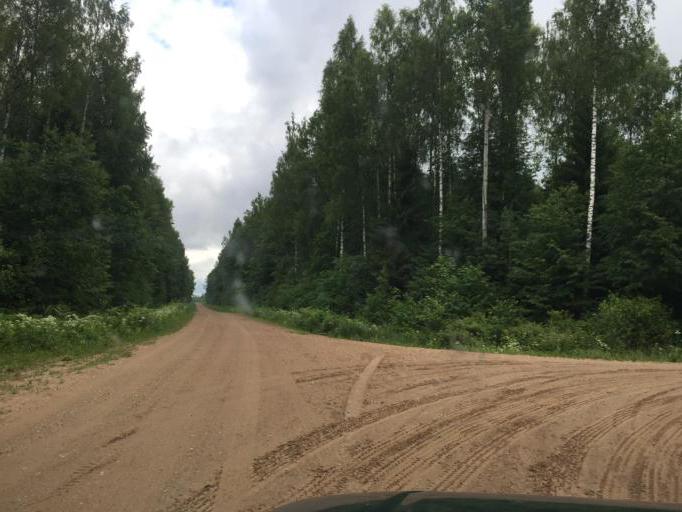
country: LV
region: Vilaka
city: Vilaka
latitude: 57.3885
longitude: 27.4893
